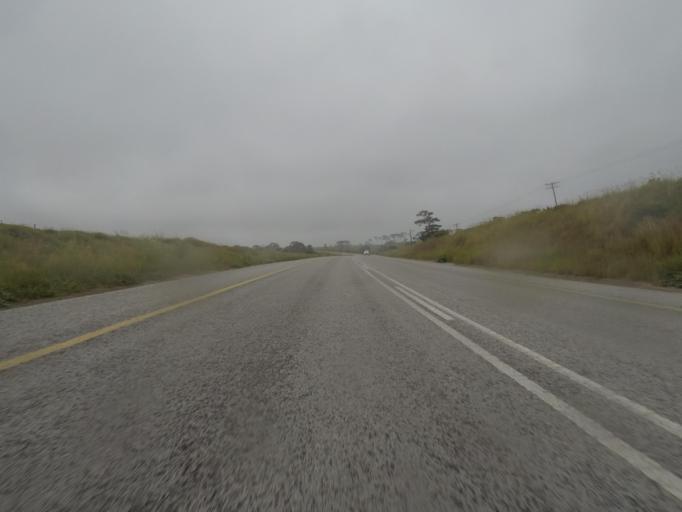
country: ZA
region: Eastern Cape
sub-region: Cacadu District Municipality
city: Grahamstown
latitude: -33.6436
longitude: 26.3506
